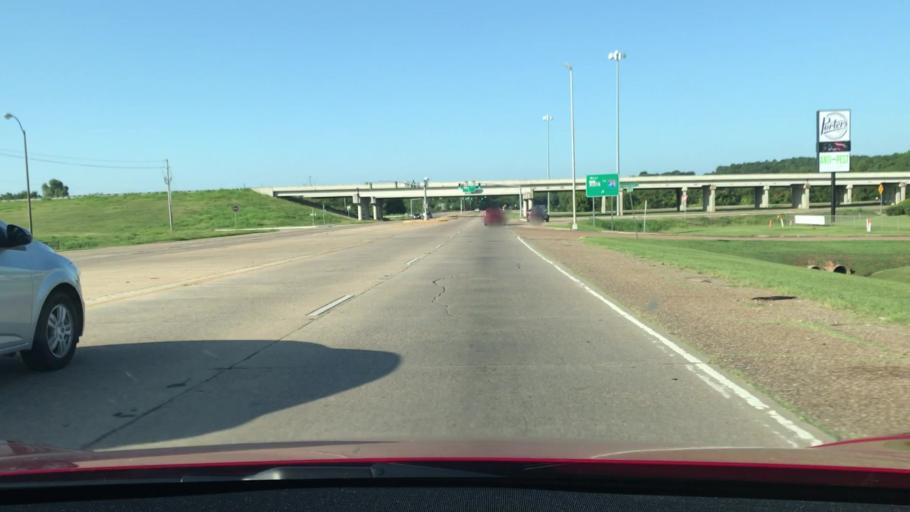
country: US
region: Louisiana
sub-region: Bossier Parish
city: Bossier City
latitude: 32.4134
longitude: -93.7241
